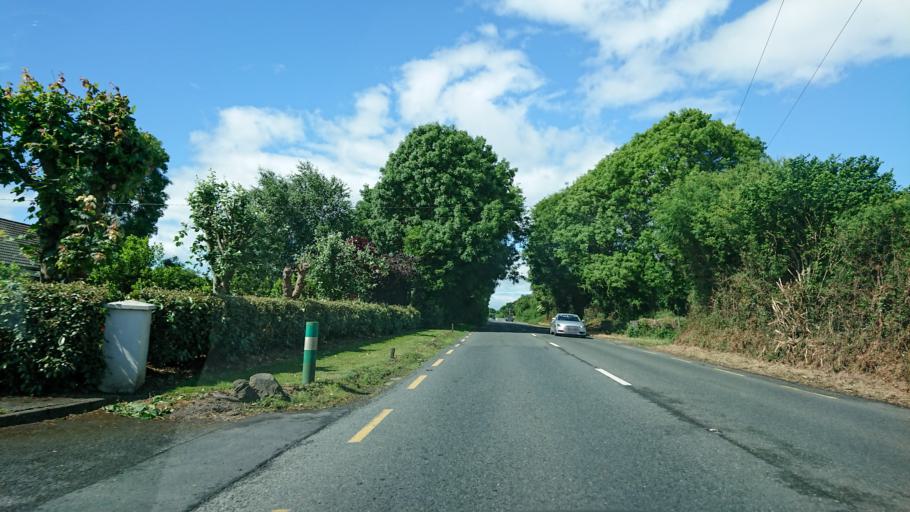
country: IE
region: Munster
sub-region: Waterford
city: Waterford
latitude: 52.2356
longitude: -7.1861
